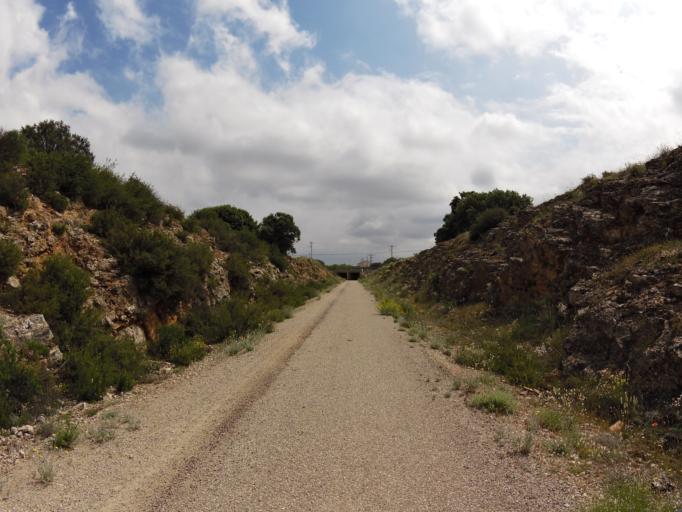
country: ES
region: Castille-La Mancha
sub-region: Provincia de Albacete
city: Robledo
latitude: 38.7682
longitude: -2.4515
